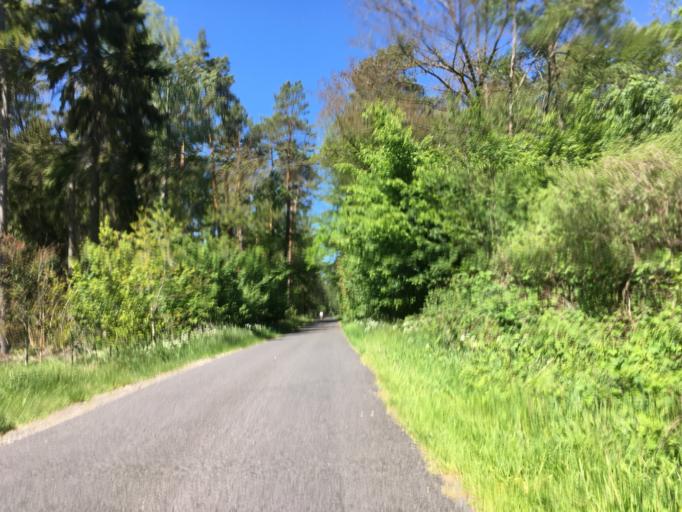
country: DE
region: Brandenburg
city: Zehdenick
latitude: 52.9851
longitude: 13.4329
